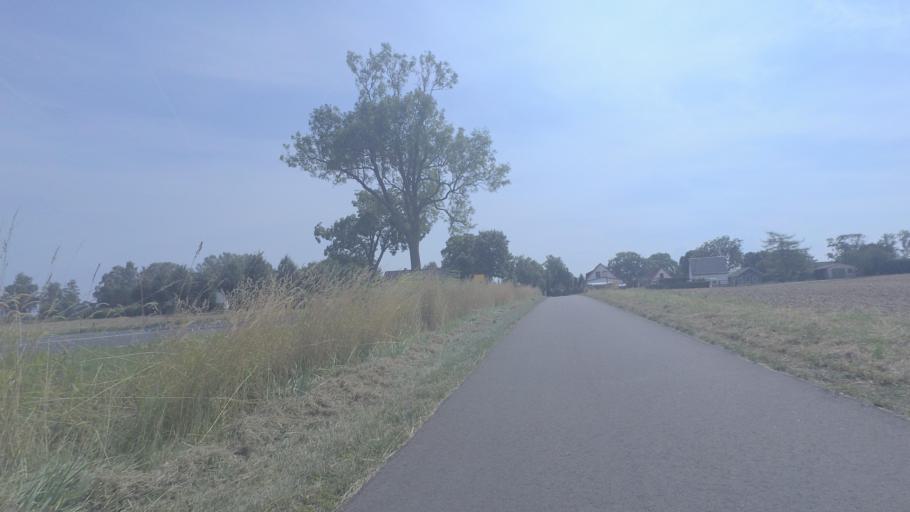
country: DE
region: Mecklenburg-Vorpommern
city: Garz
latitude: 54.2626
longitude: 13.3505
